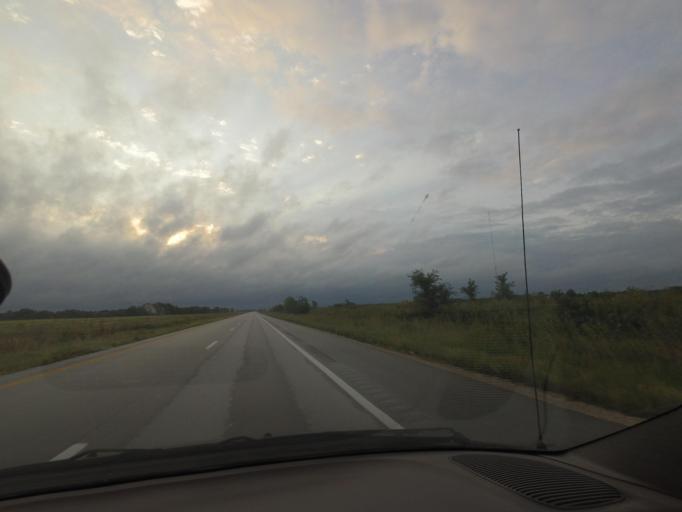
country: US
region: Missouri
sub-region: Shelby County
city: Shelbina
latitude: 39.6801
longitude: -91.9821
